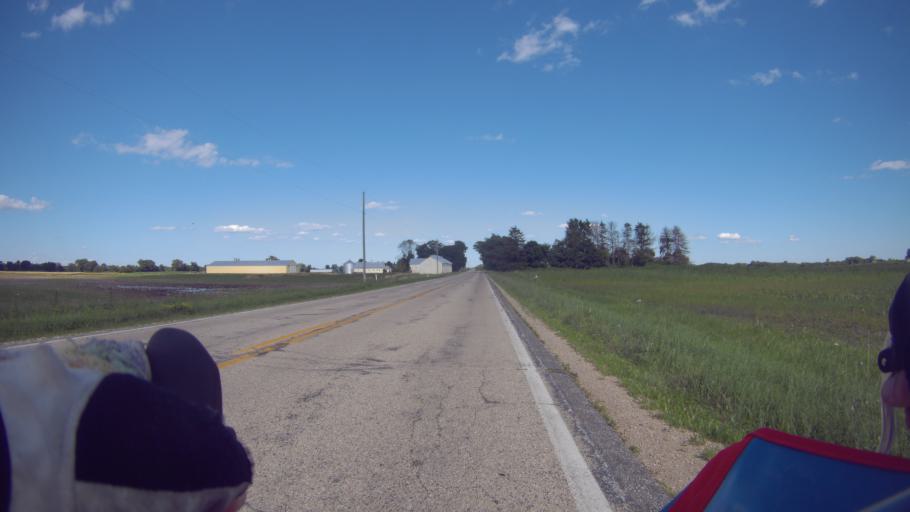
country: US
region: Wisconsin
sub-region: Dane County
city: Stoughton
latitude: 42.8930
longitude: -89.2745
